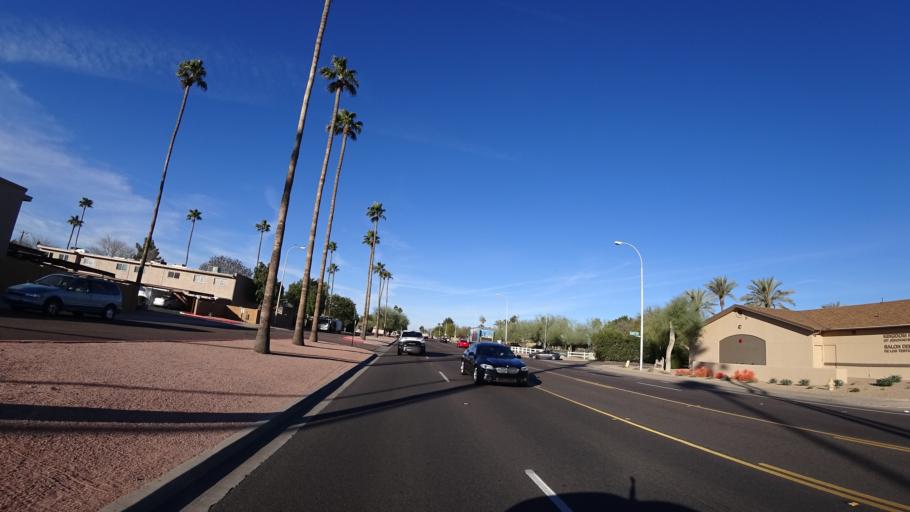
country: US
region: Arizona
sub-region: Maricopa County
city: Scottsdale
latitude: 33.4803
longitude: -111.9028
